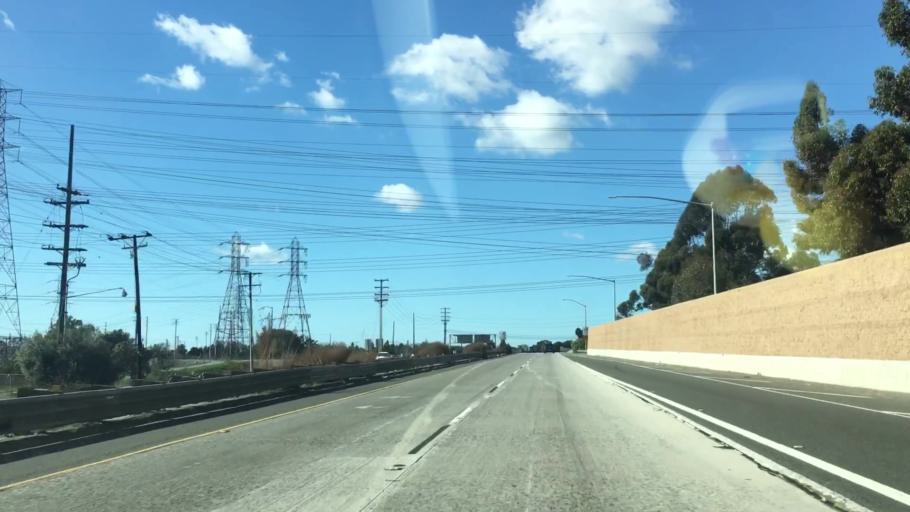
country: US
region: California
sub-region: Orange County
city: Rossmoor
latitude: 33.7744
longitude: -118.0952
